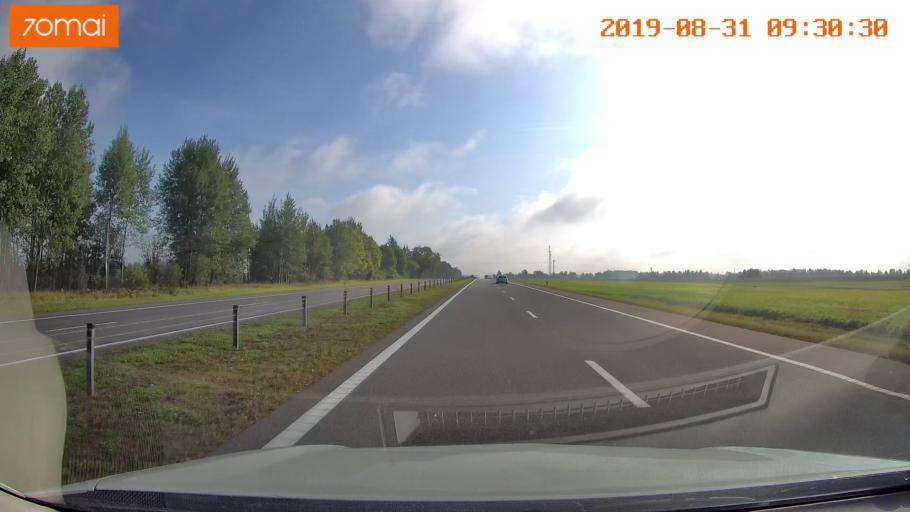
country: BY
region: Minsk
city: Byerazino
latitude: 53.8533
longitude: 29.1255
